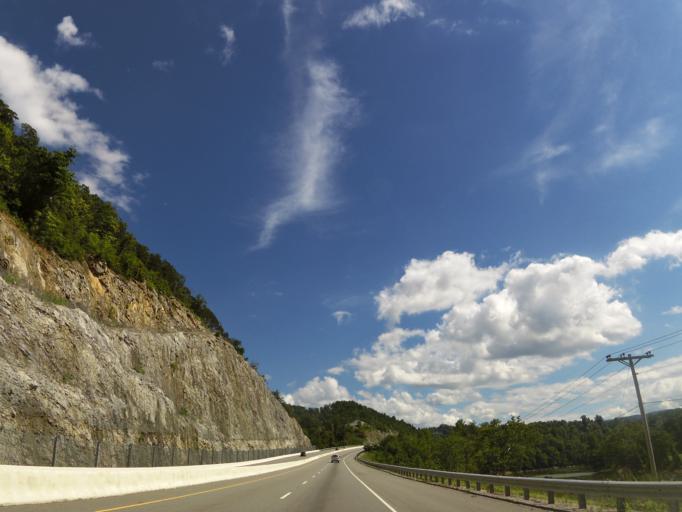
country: US
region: Tennessee
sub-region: Grainger County
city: Rutledge
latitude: 36.3932
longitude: -83.4495
